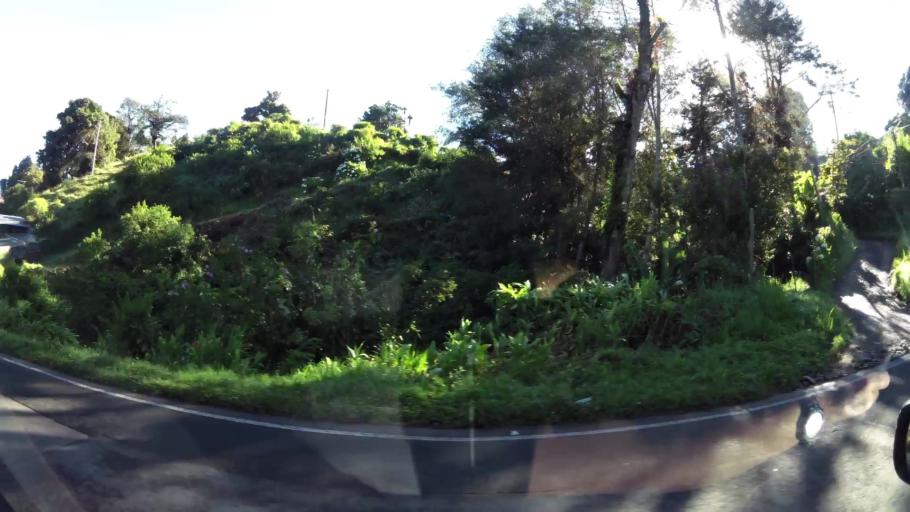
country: CR
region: San Jose
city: San Marcos
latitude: 9.7210
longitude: -83.9497
